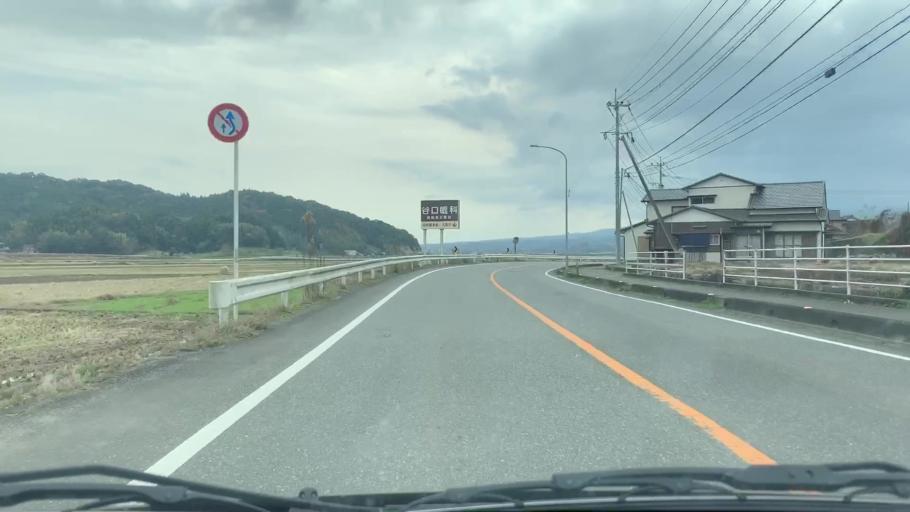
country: JP
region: Saga Prefecture
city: Kashima
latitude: 33.1443
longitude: 130.0637
